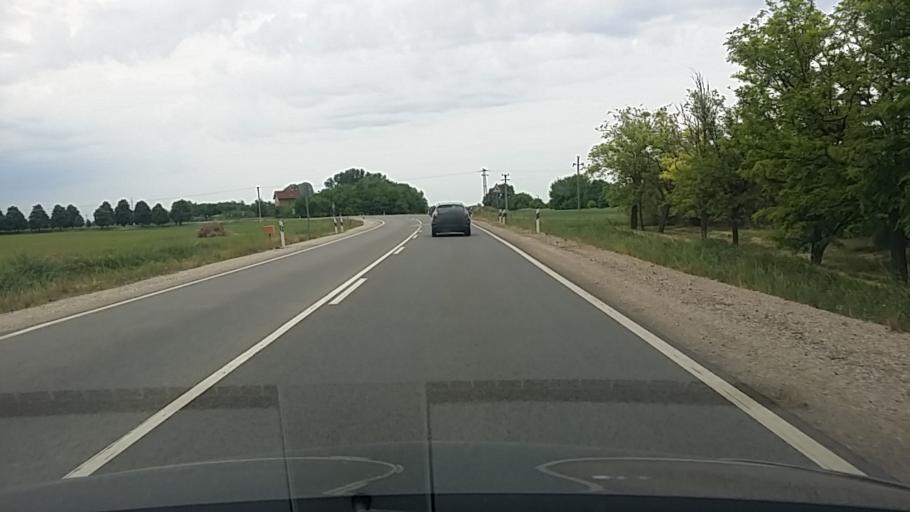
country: HU
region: Fejer
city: dunaujvaros
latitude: 46.9851
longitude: 18.9012
